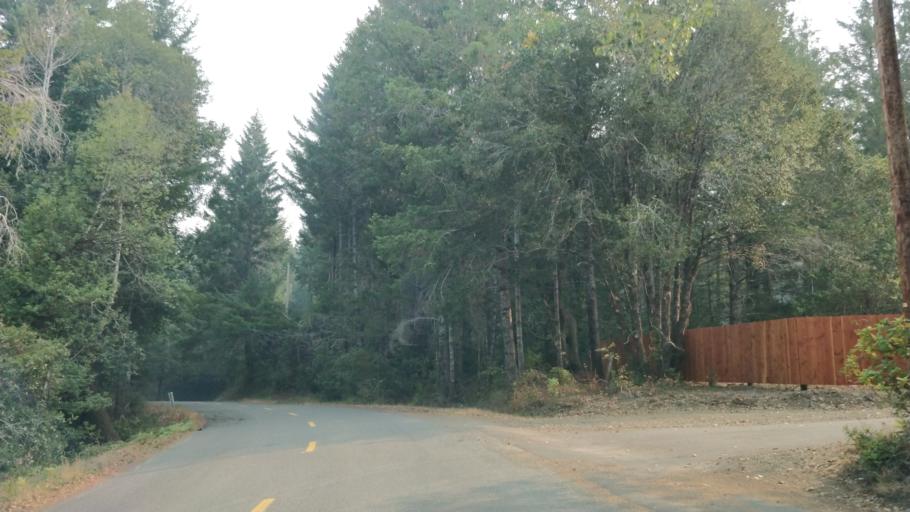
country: US
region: California
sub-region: Humboldt County
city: Rio Dell
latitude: 40.2328
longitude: -124.1544
